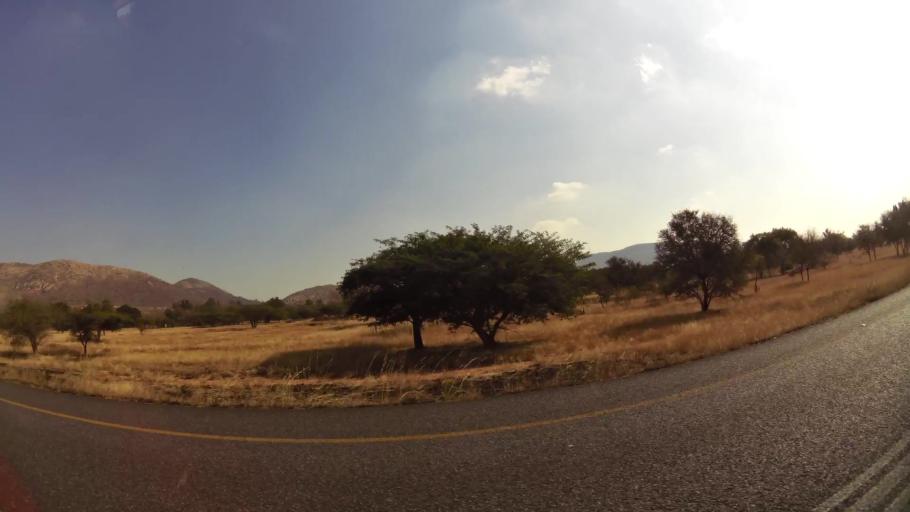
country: ZA
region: North-West
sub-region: Bojanala Platinum District Municipality
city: Rustenburg
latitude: -25.6279
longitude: 27.1577
